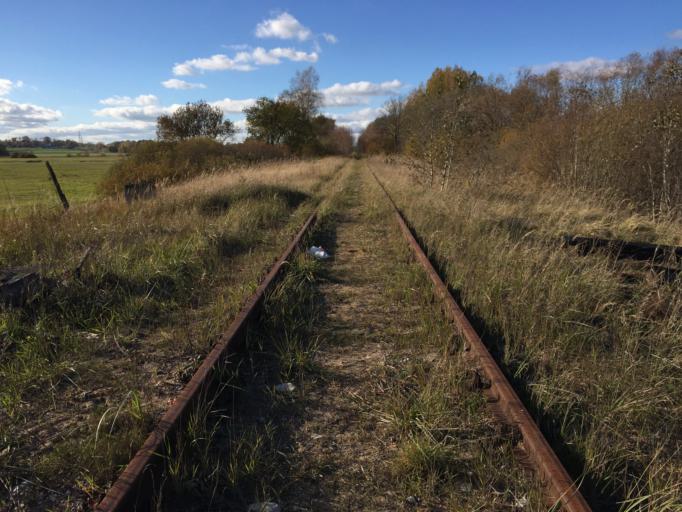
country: LV
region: Tukuma Rajons
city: Tukums
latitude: 56.9601
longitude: 23.1027
